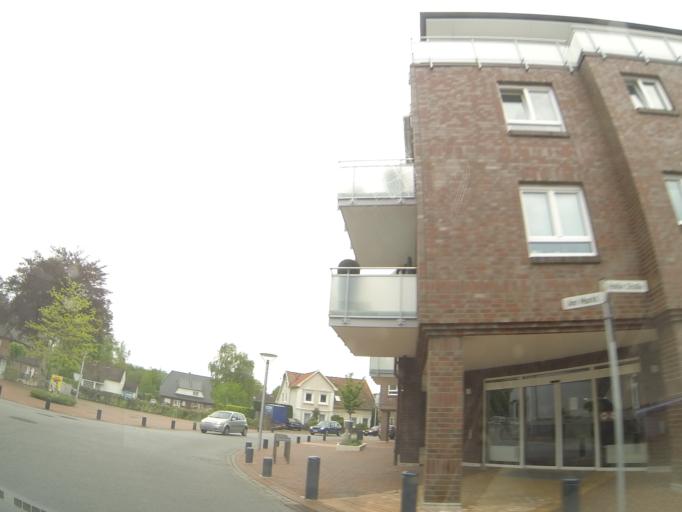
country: DE
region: Schleswig-Holstein
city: Rellingen
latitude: 53.6496
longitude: 9.8283
